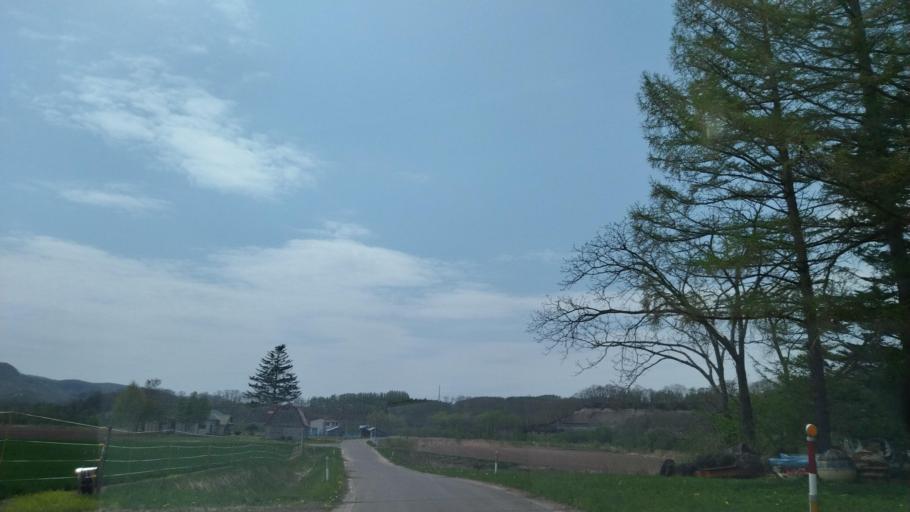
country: JP
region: Hokkaido
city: Otofuke
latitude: 43.3182
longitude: 143.5753
